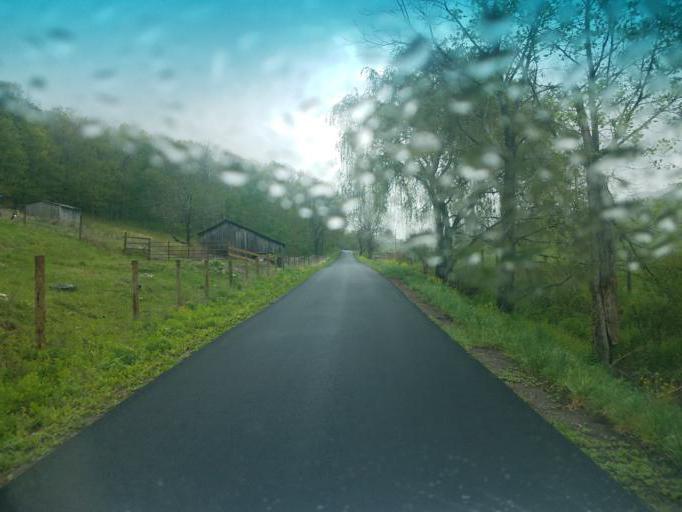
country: US
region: Virginia
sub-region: Smyth County
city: Marion
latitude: 36.9268
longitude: -81.5473
